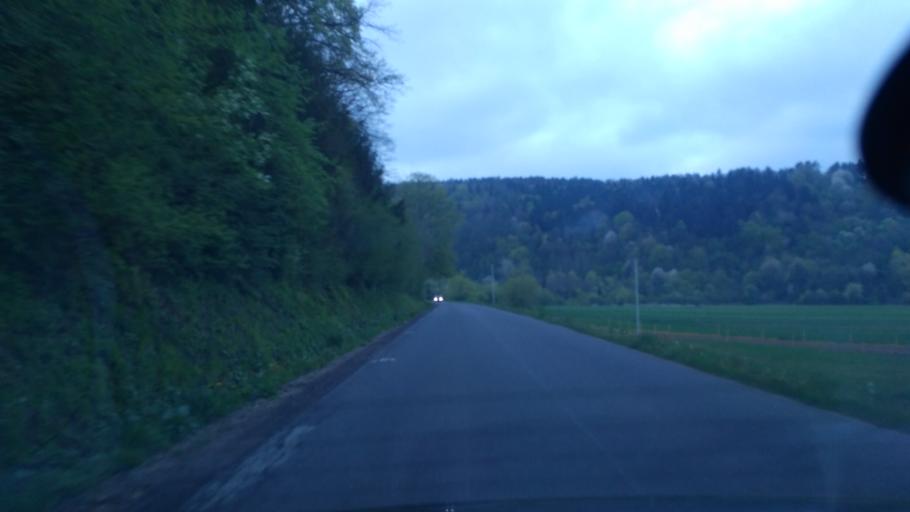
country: PL
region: Subcarpathian Voivodeship
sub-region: Powiat brzozowski
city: Nozdrzec
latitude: 49.7258
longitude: 22.2215
